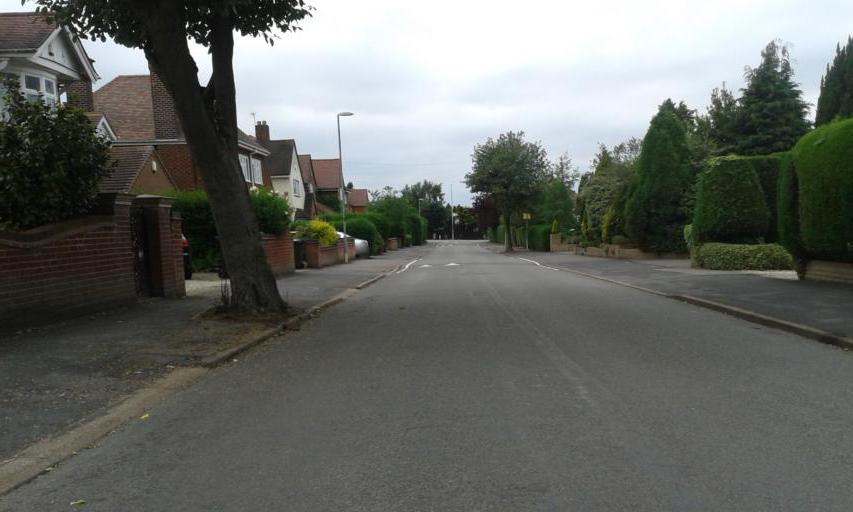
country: GB
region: England
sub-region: Leicestershire
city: Hinckley
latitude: 52.5492
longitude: -1.3549
